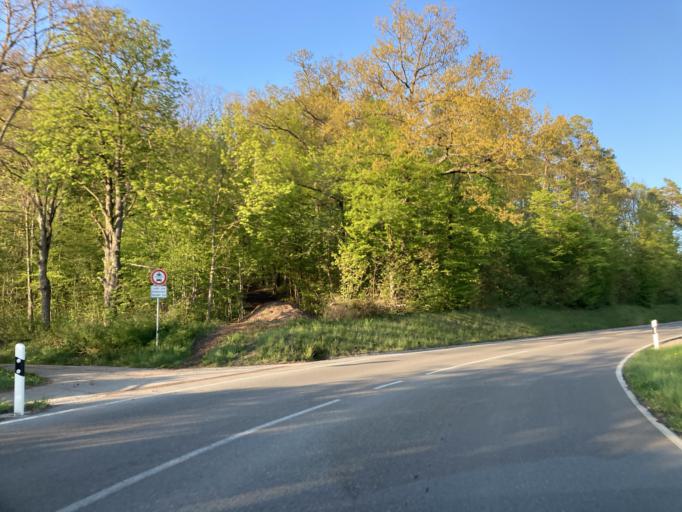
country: DE
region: Baden-Wuerttemberg
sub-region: Regierungsbezirk Stuttgart
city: Nufringen
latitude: 48.6018
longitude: 8.8874
